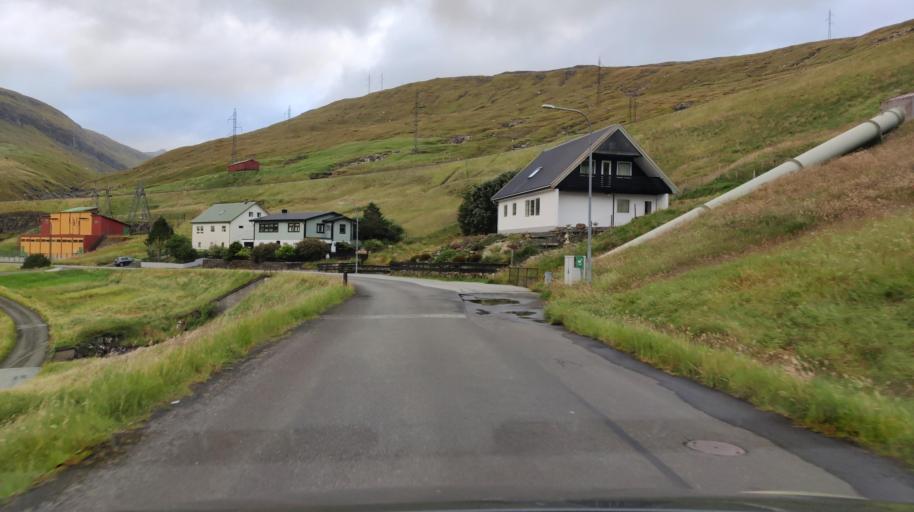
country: FO
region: Streymoy
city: Vestmanna
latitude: 62.1503
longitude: -7.1482
